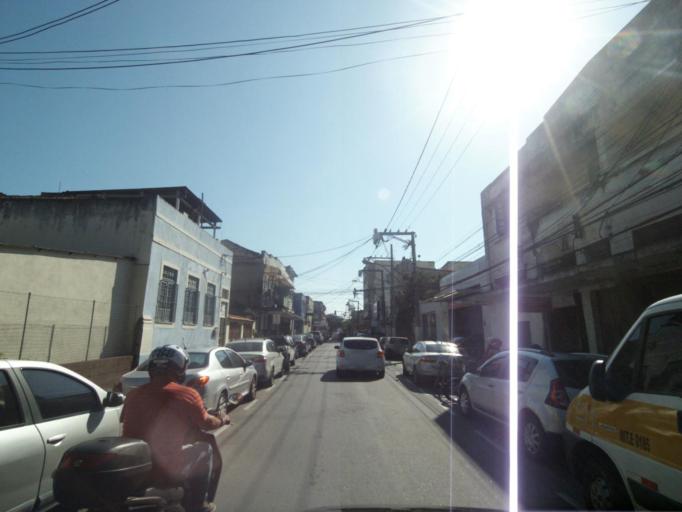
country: BR
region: Rio de Janeiro
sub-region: Niteroi
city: Niteroi
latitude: -22.8879
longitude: -43.1197
